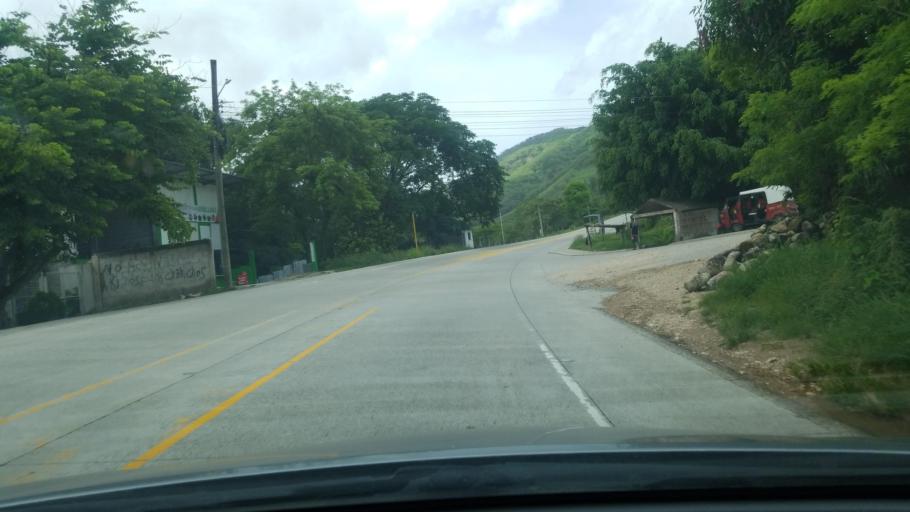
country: HN
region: Copan
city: San Juan de Planes
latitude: 14.9331
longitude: -88.7648
